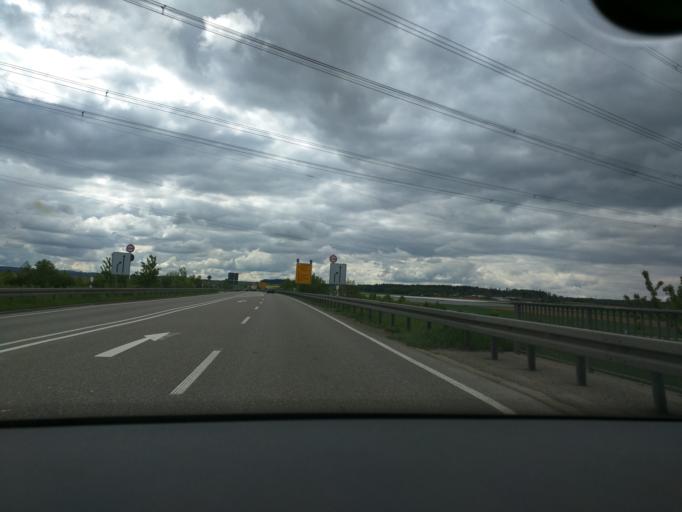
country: DE
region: Baden-Wuerttemberg
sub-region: Regierungsbezirk Stuttgart
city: Bondorf
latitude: 48.5068
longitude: 8.8228
